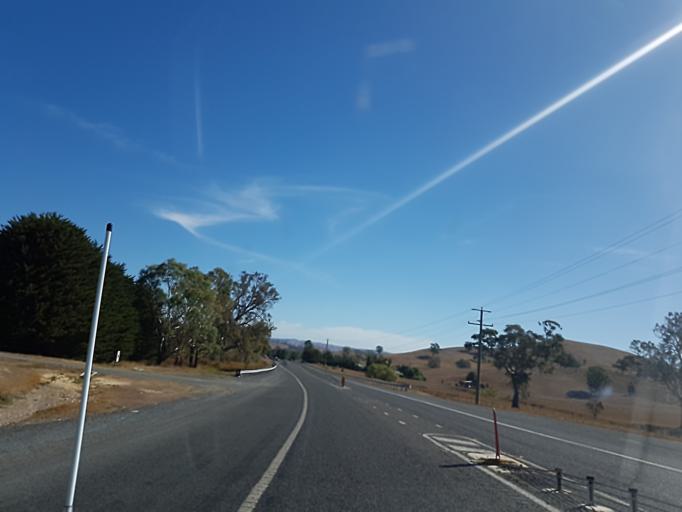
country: AU
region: Victoria
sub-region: Murrindindi
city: Alexandra
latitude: -37.2014
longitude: 145.4669
